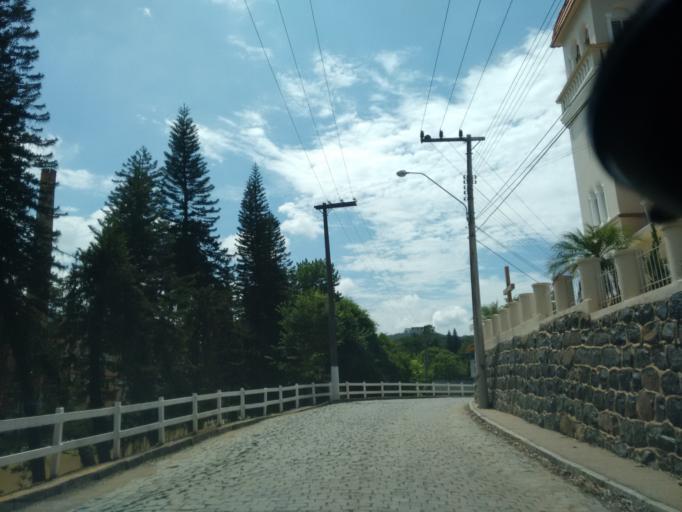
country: BR
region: Santa Catarina
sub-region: Indaial
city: Indaial
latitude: -26.8534
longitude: -49.1551
